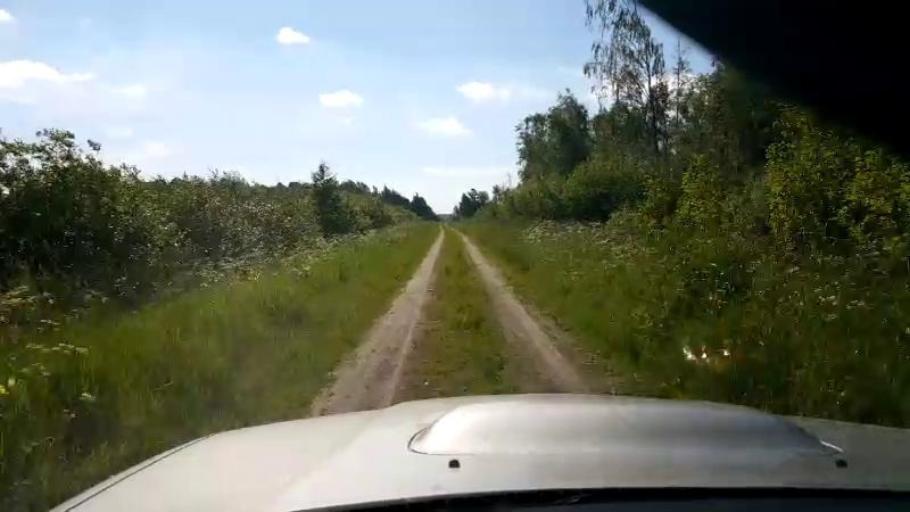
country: EE
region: Paernumaa
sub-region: Sindi linn
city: Sindi
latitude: 58.5033
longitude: 24.6426
